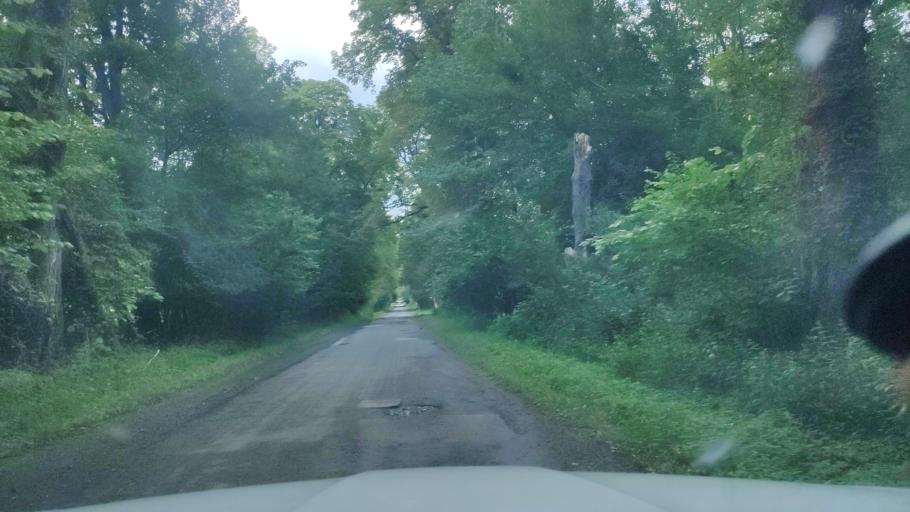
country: HU
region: Heves
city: Parad
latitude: 47.9069
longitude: 20.0557
